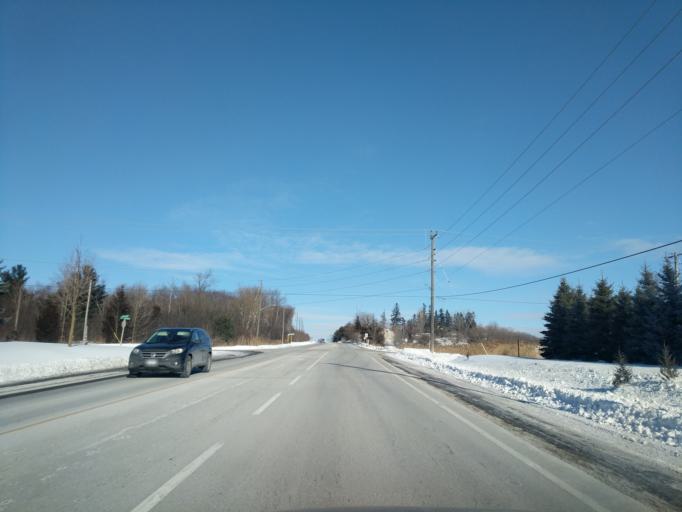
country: CA
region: Ontario
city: Pickering
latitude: 43.8506
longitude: -79.1513
